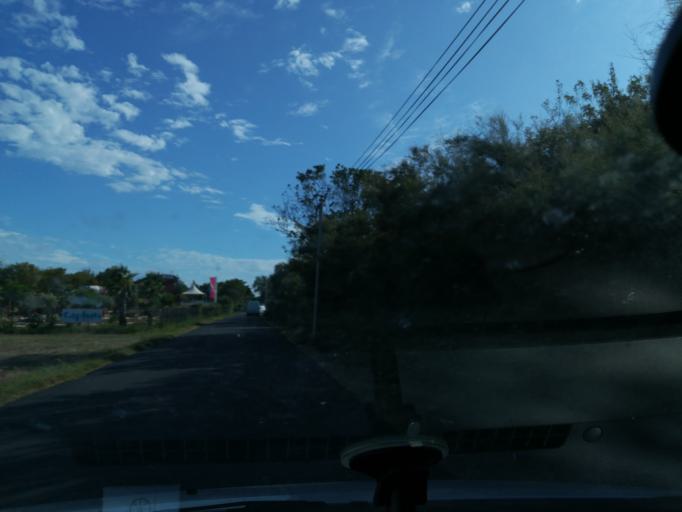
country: FR
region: Languedoc-Roussillon
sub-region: Departement de l'Herault
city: Vias
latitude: 43.2981
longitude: 3.4009
